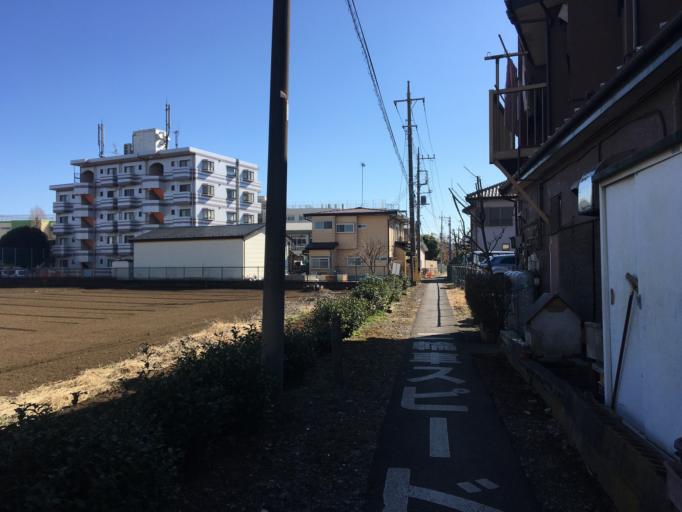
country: JP
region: Saitama
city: Kamifukuoka
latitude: 35.8722
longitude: 139.5038
